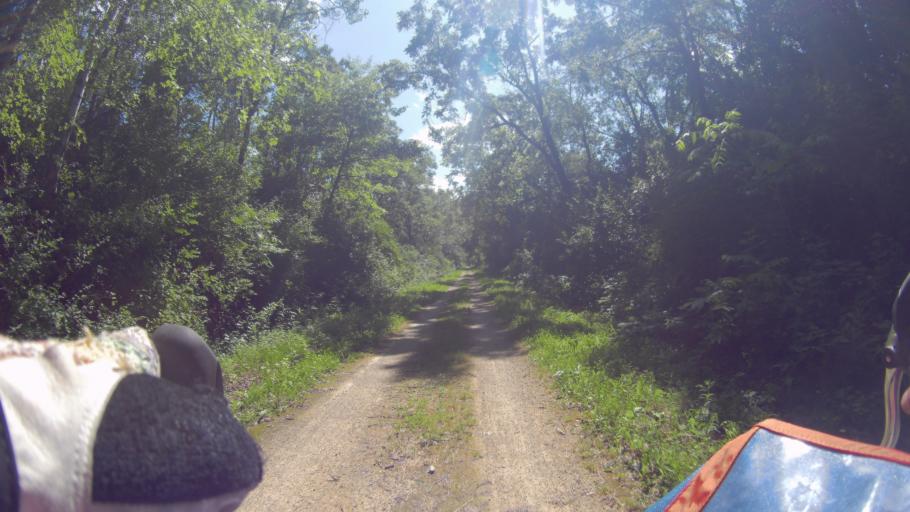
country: US
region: Wisconsin
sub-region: Dane County
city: Fitchburg
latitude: 42.9376
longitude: -89.4922
